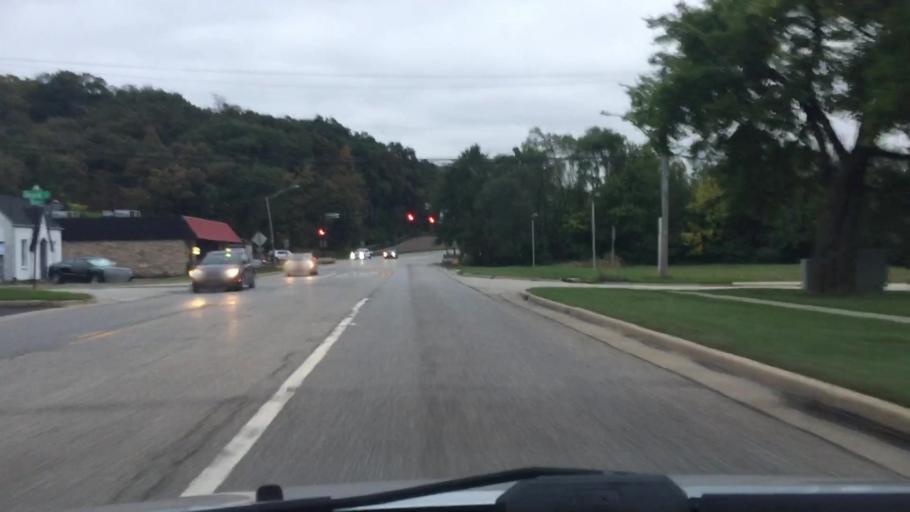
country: US
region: Illinois
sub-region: McHenry County
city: Algonquin
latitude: 42.1570
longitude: -88.2967
